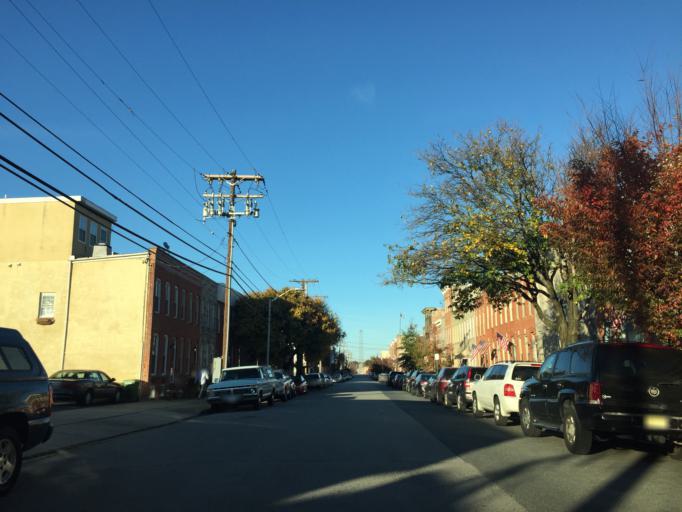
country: US
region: Maryland
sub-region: City of Baltimore
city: Baltimore
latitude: 39.2707
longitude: -76.5927
